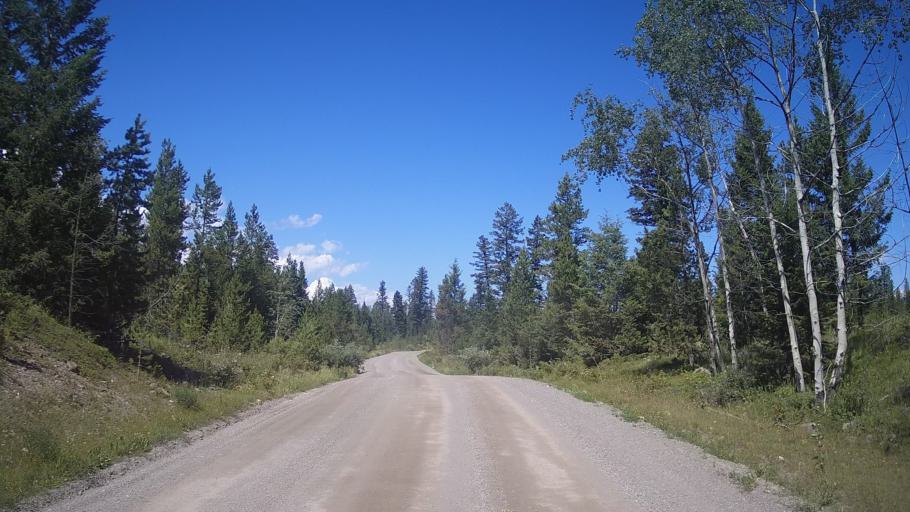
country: CA
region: British Columbia
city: Cache Creek
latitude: 51.1621
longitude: -121.5579
